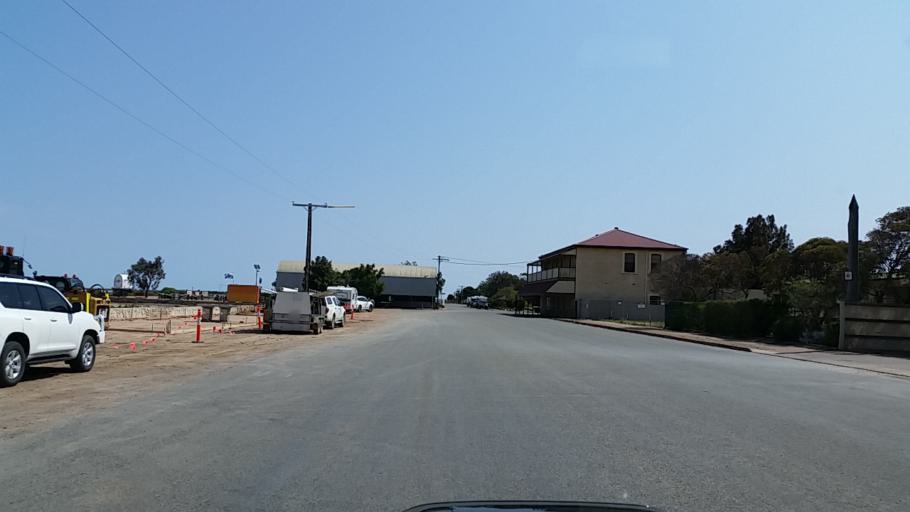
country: AU
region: South Australia
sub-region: Port Pirie City and Dists
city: Port Pirie
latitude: -33.0230
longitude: 138.0000
